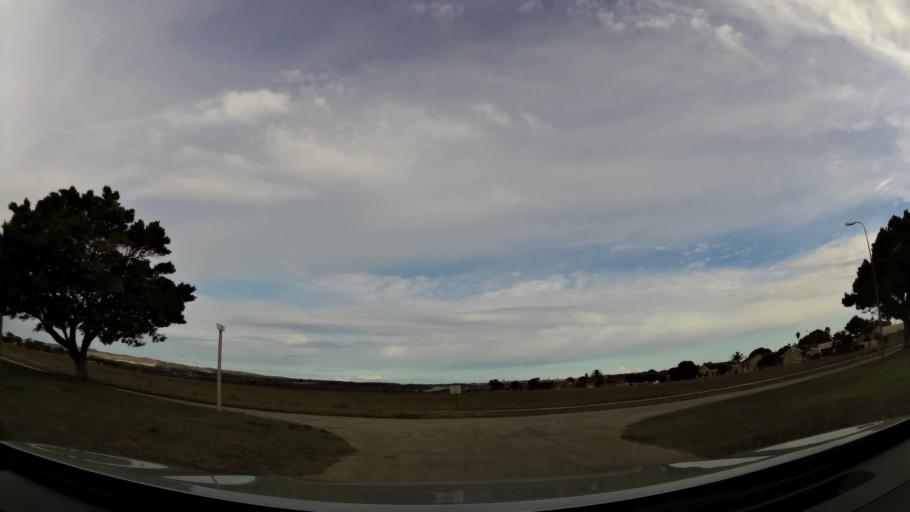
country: ZA
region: Eastern Cape
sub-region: Nelson Mandela Bay Metropolitan Municipality
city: Port Elizabeth
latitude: -33.9363
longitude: 25.4681
